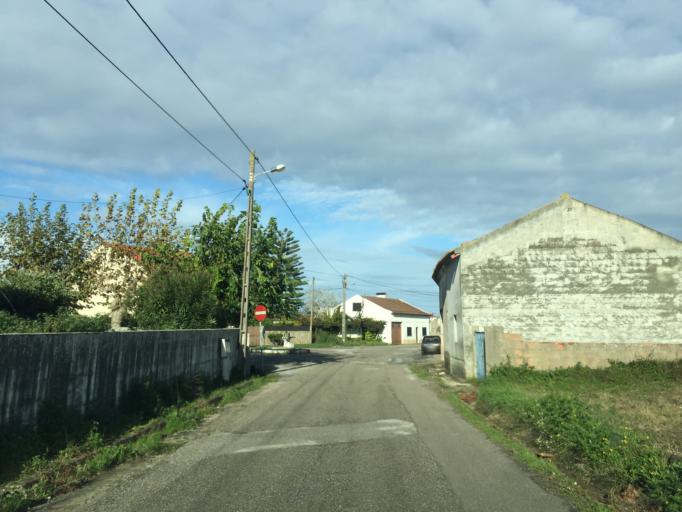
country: PT
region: Coimbra
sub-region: Figueira da Foz
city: Lavos
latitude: 40.0646
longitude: -8.8188
